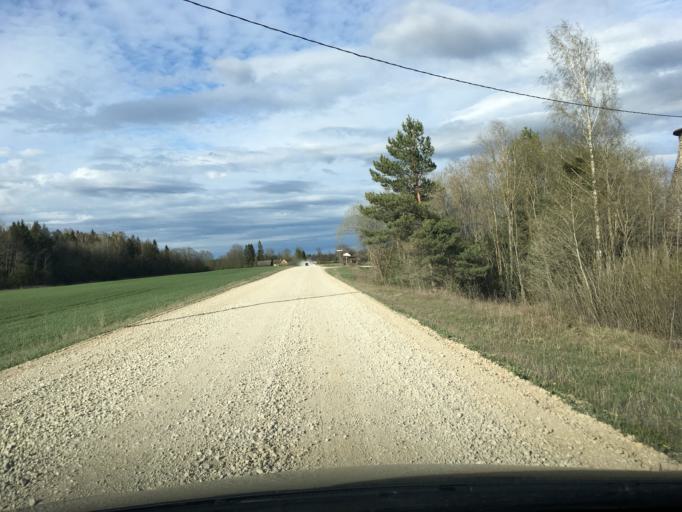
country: EE
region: Raplamaa
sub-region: Maerjamaa vald
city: Marjamaa
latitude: 58.9742
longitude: 24.3486
